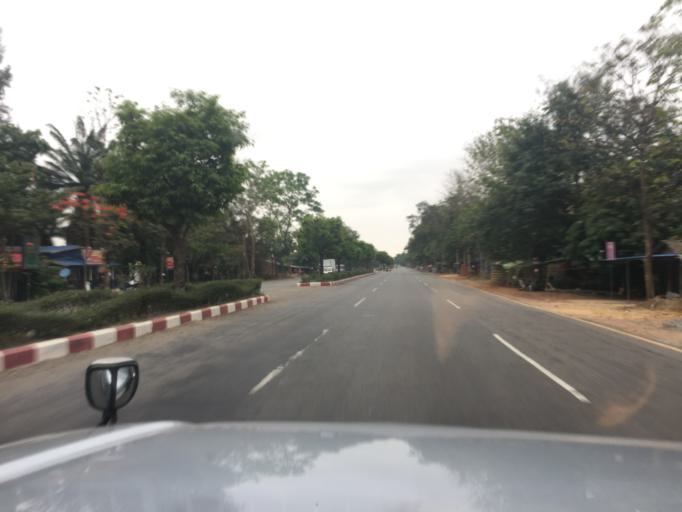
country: MM
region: Bago
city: Bago
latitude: 17.2236
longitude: 96.4459
